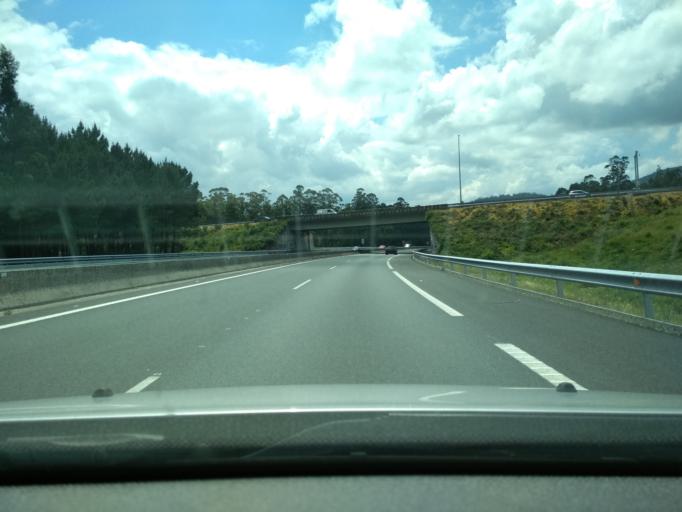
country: ES
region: Galicia
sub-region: Provincia de Pontevedra
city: Barro
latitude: 42.5194
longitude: -8.6647
